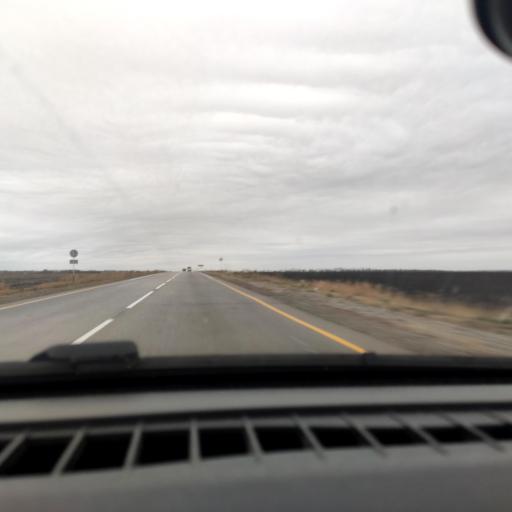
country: RU
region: Voronezj
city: Strelitsa
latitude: 51.4673
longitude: 38.9605
